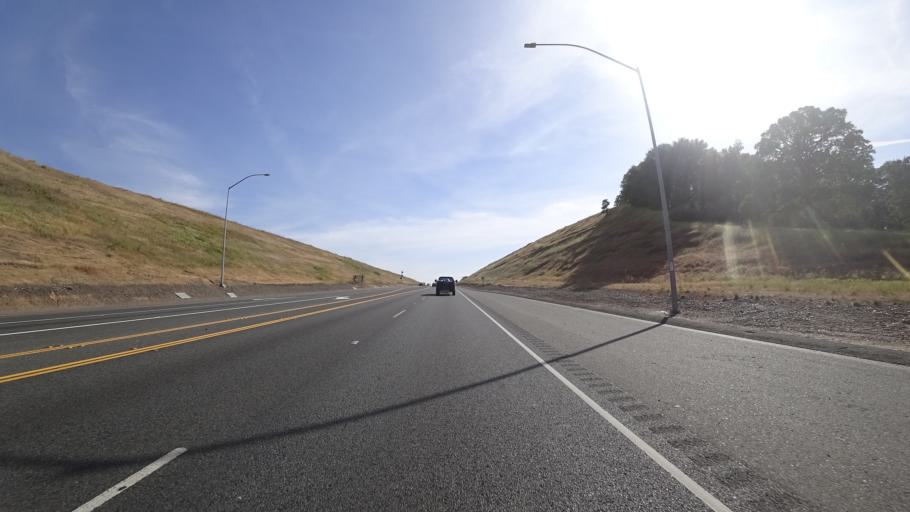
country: US
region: California
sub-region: Butte County
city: South Oroville
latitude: 39.4633
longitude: -121.5796
